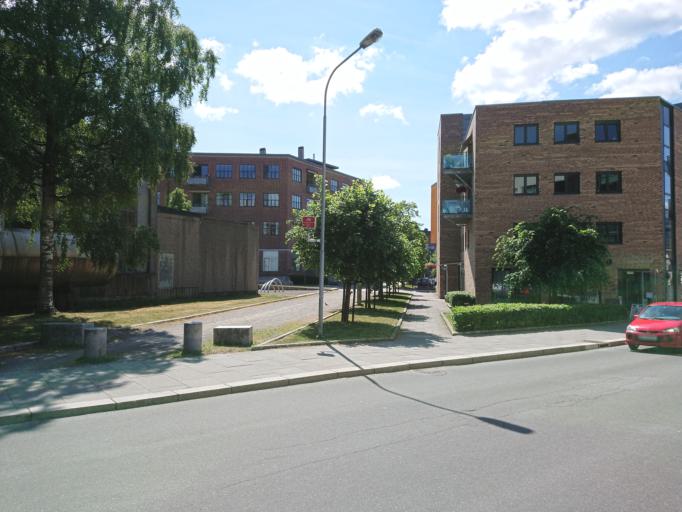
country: NO
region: Ostfold
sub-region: Askim
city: Askim
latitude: 59.5844
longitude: 11.1643
